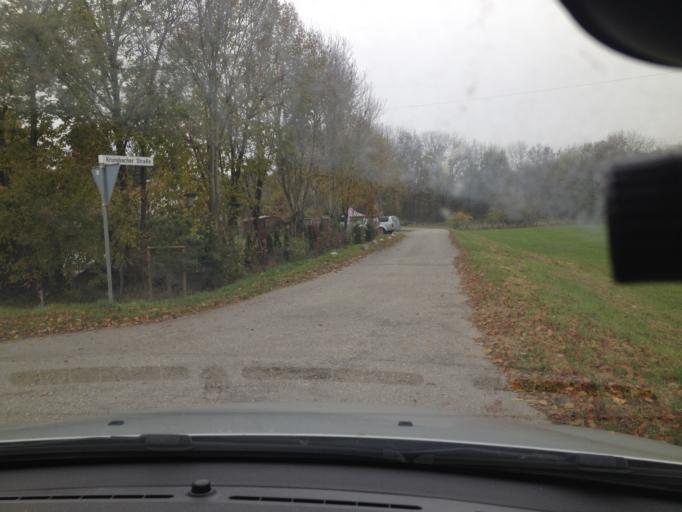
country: DE
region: Bavaria
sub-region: Swabia
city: Hiltenfingen
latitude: 48.1917
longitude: 10.7305
